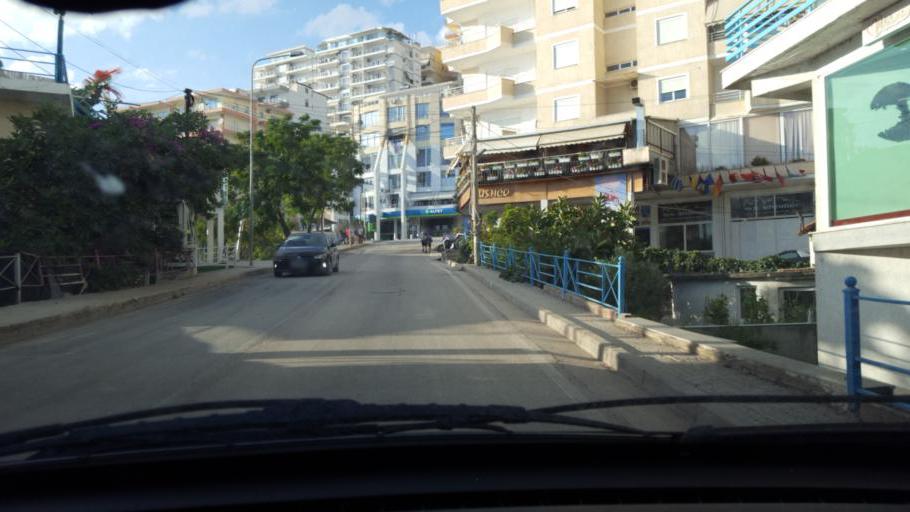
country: AL
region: Vlore
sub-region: Rrethi i Sarandes
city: Sarande
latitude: 39.8722
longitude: 20.0137
